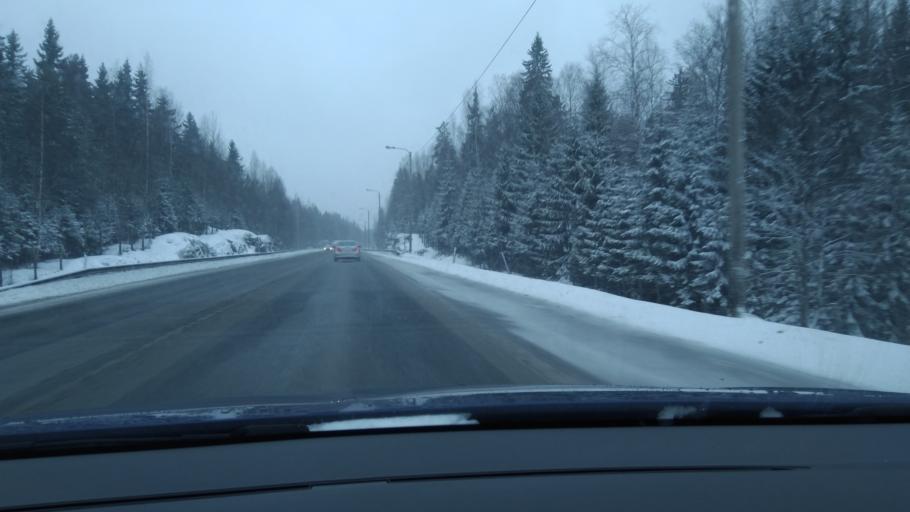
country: FI
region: Pirkanmaa
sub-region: Tampere
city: Tampere
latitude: 61.5150
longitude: 23.9148
